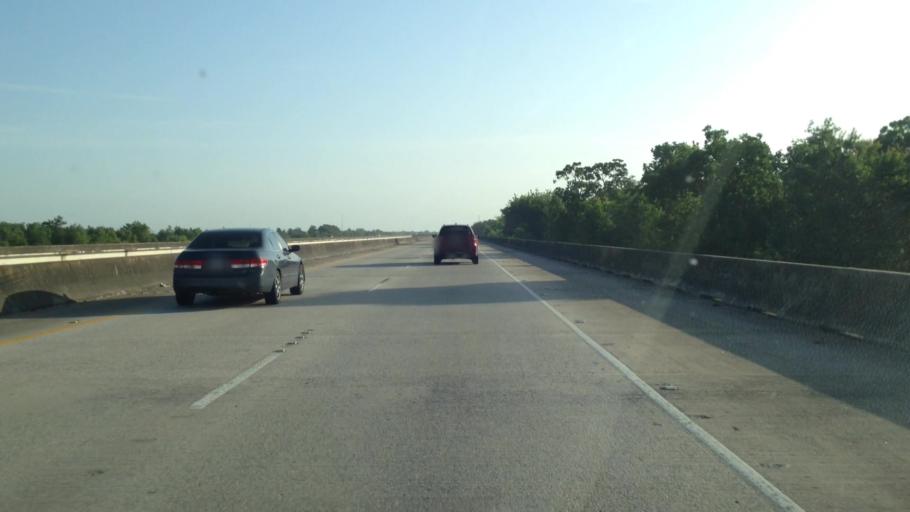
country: US
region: Louisiana
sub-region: Saint John the Baptist Parish
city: Laplace
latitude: 30.2439
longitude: -90.4062
